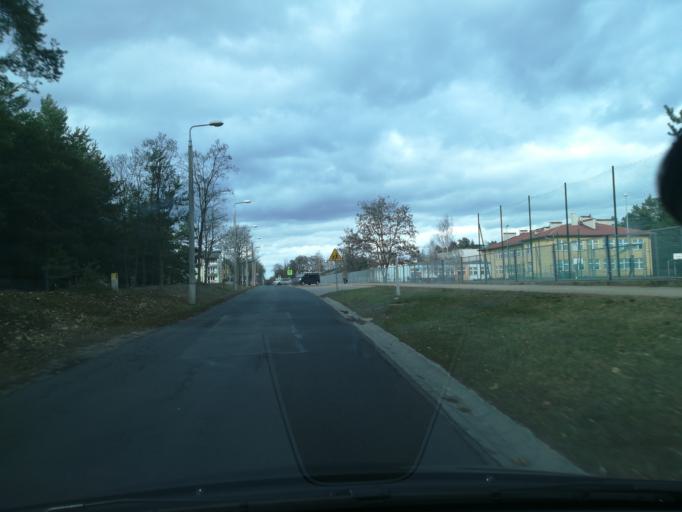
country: PL
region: Kujawsko-Pomorskie
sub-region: Powiat torunski
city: Lubicz Dolny
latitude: 52.9795
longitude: 18.6851
